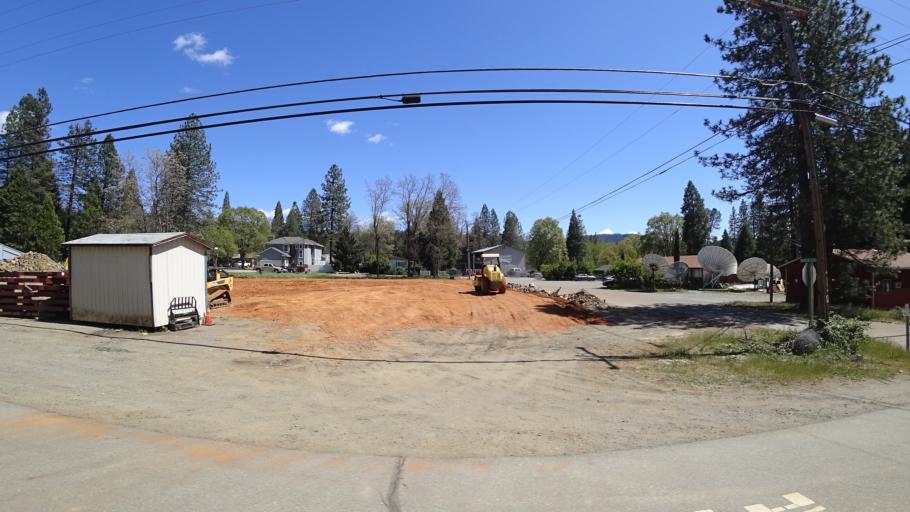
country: US
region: California
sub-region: Trinity County
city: Weaverville
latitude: 40.7364
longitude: -122.9301
